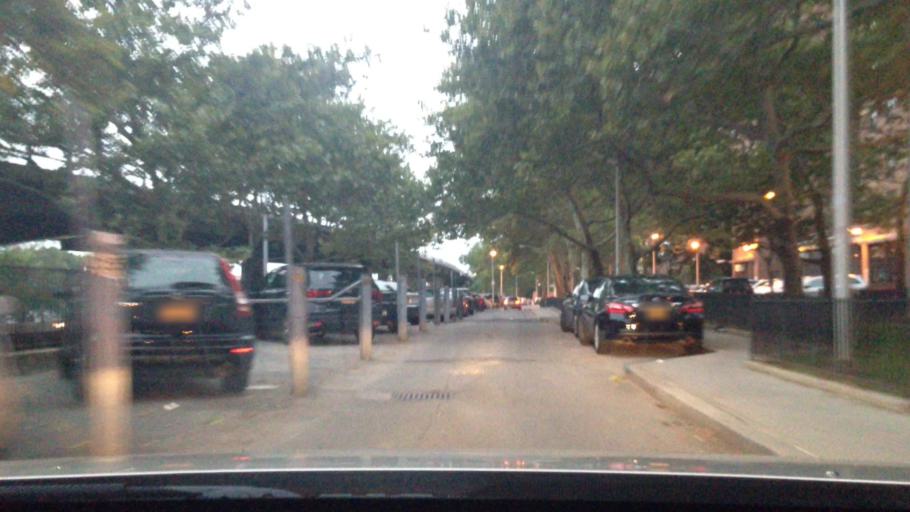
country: US
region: New York
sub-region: New York County
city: Inwood
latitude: 40.8338
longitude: -73.9357
